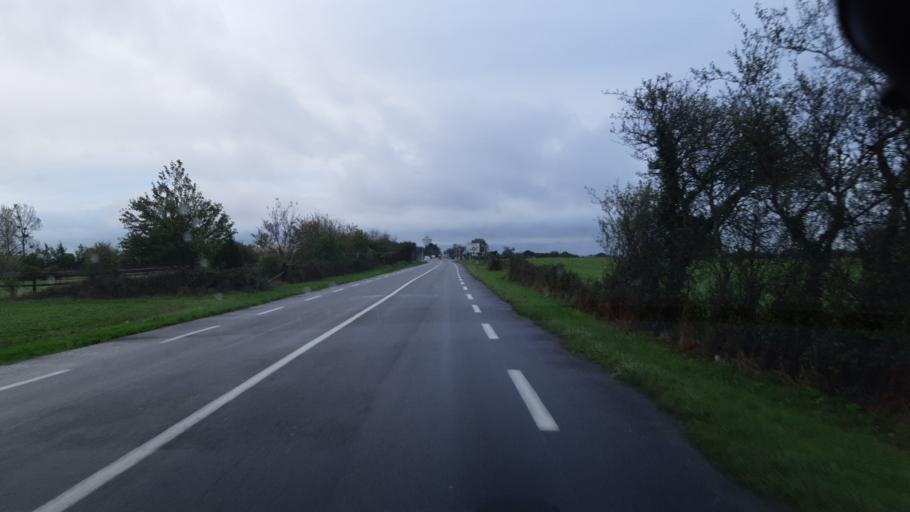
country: FR
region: Lower Normandy
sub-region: Departement de la Manche
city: Donville-les-Bains
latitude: 48.8607
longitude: -1.5510
